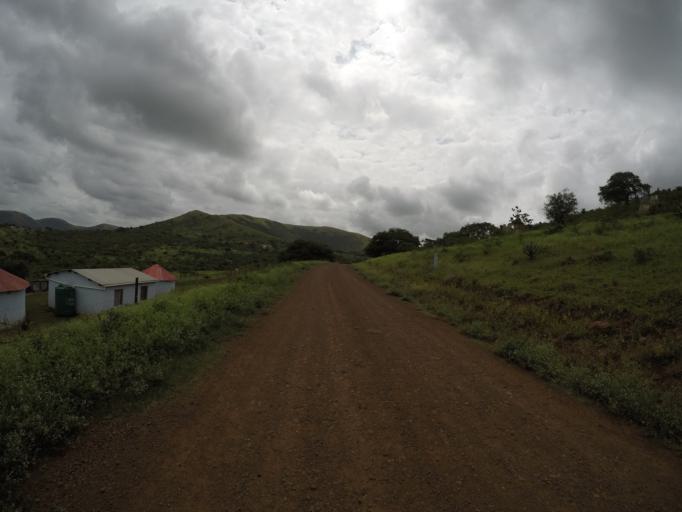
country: ZA
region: KwaZulu-Natal
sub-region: uThungulu District Municipality
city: Empangeni
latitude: -28.6155
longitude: 31.8945
